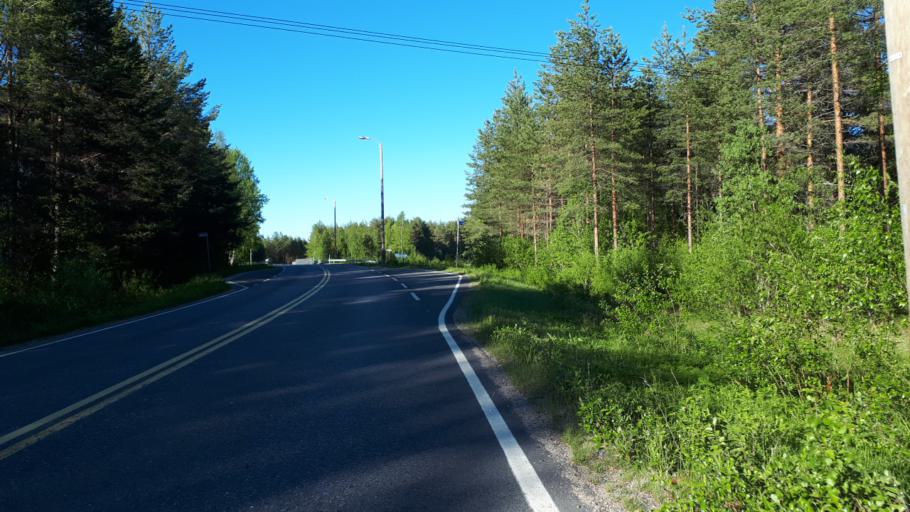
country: FI
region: Northern Ostrobothnia
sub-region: Oulunkaari
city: Ii
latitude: 65.3262
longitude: 25.5188
